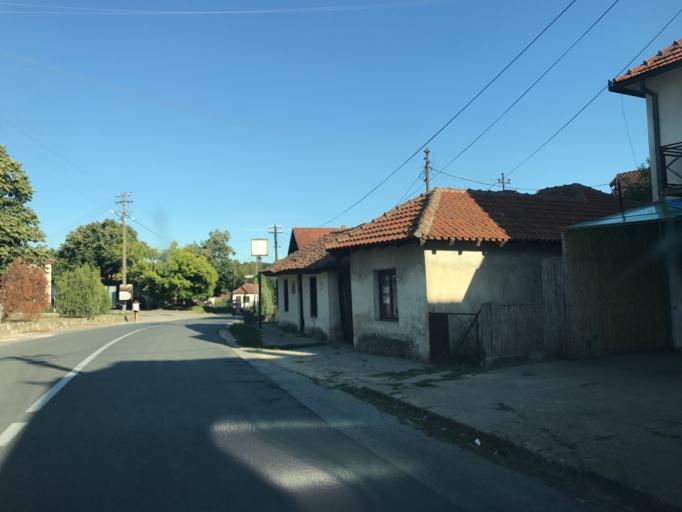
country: RO
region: Mehedinti
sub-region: Comuna Gogosu
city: Ostrovu Mare
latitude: 44.2910
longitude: 22.3522
